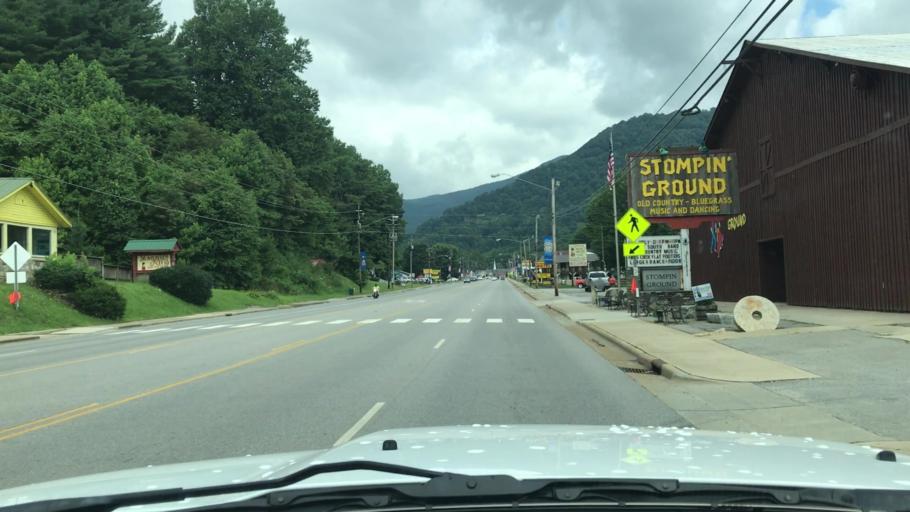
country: US
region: North Carolina
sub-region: Haywood County
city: Maggie Valley
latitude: 35.5136
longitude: -83.0805
